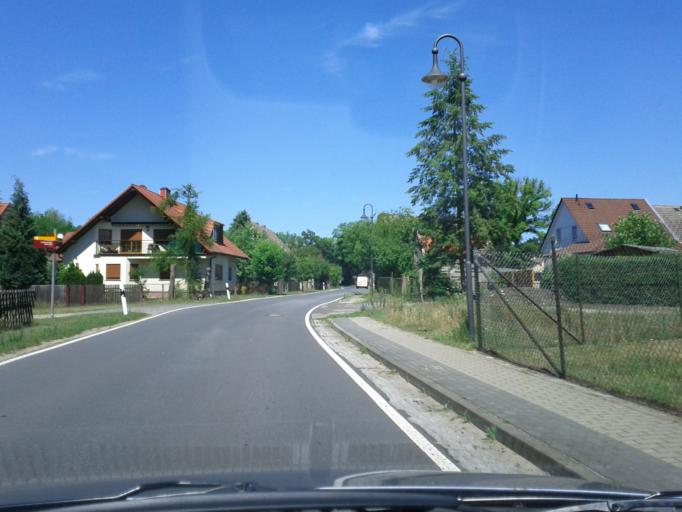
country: DE
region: Brandenburg
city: Rehfelde
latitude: 52.4526
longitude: 13.9553
